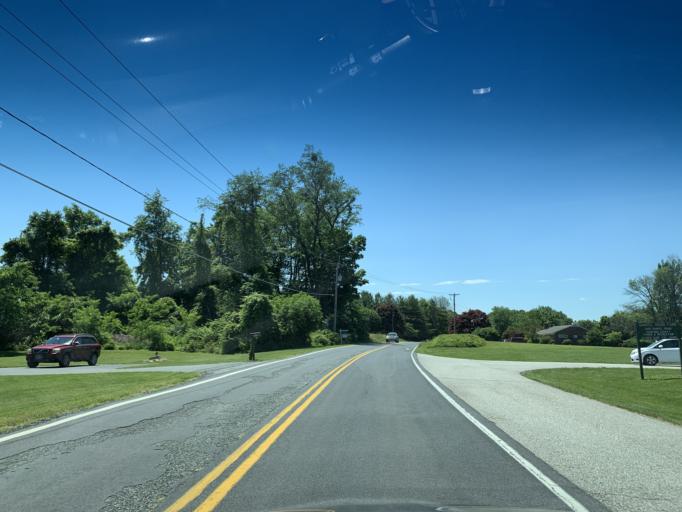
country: US
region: Maryland
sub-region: Harford County
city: Aberdeen
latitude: 39.5536
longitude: -76.1466
